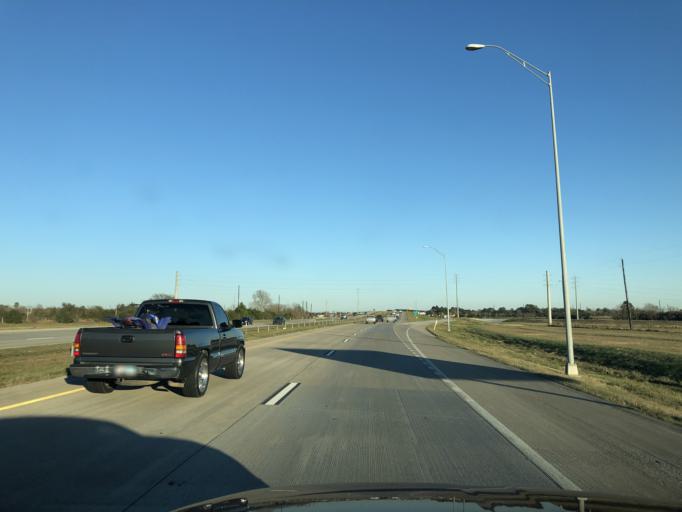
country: US
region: Texas
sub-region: Harris County
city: Cypress
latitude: 30.0532
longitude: -95.7406
